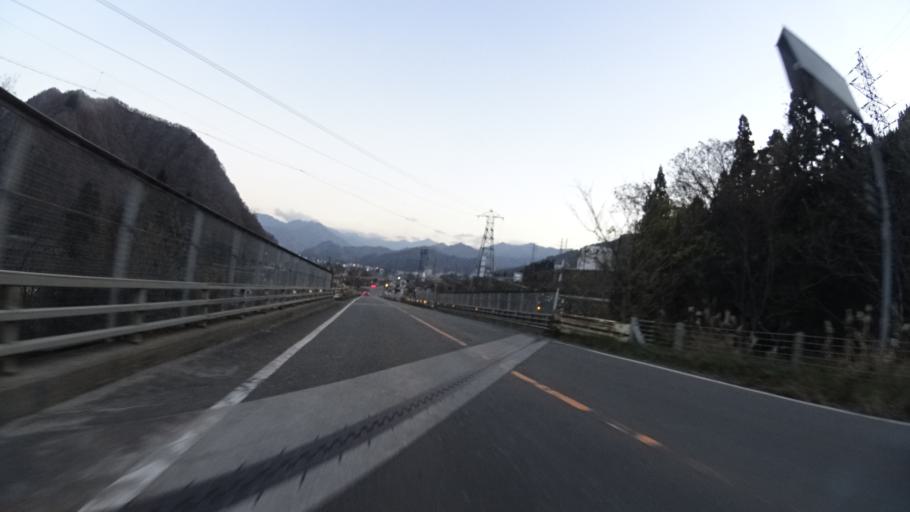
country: JP
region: Niigata
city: Shiozawa
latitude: 36.9544
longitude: 138.7994
